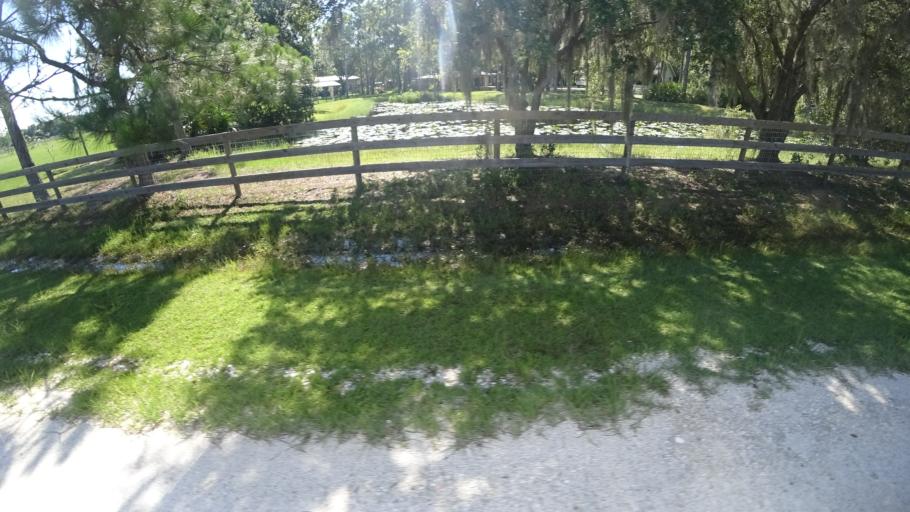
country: US
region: Florida
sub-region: Sarasota County
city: The Meadows
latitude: 27.4338
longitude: -82.3201
